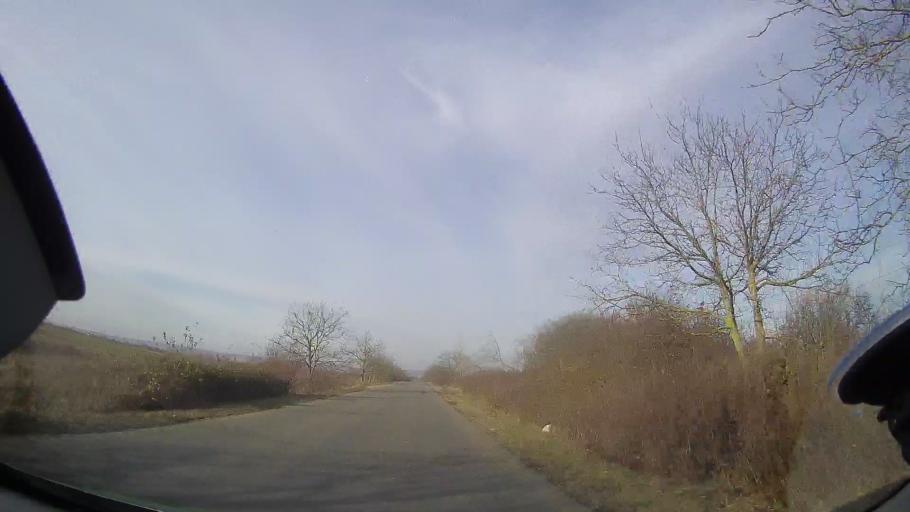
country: RO
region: Bihor
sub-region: Comuna Spinus
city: Spinus
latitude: 47.2225
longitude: 22.1704
